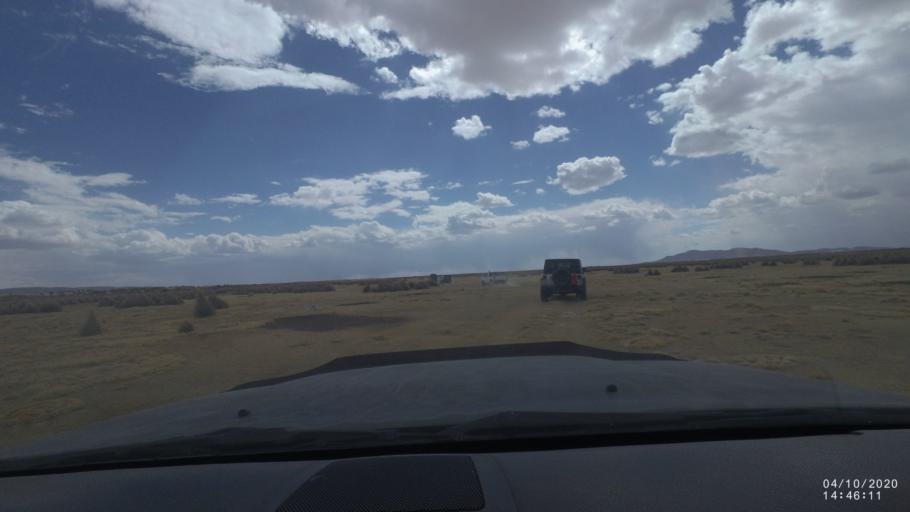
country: BO
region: Oruro
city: Poopo
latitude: -18.6866
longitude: -67.5011
